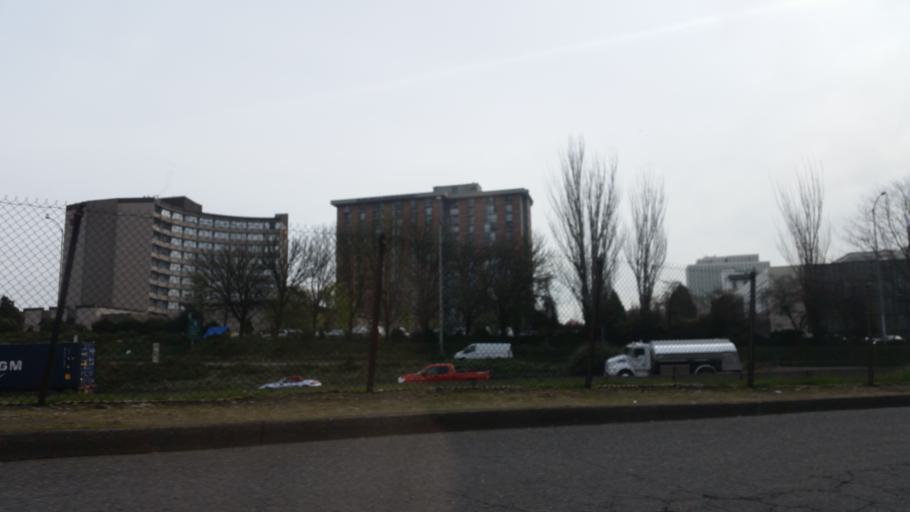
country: US
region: Oregon
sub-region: Multnomah County
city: Portland
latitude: 45.5328
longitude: -122.6661
